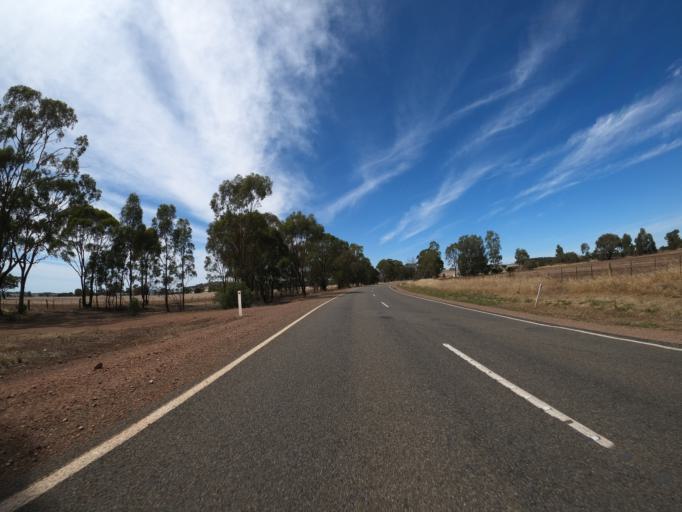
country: AU
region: Victoria
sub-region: Benalla
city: Benalla
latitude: -36.3070
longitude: 145.9581
